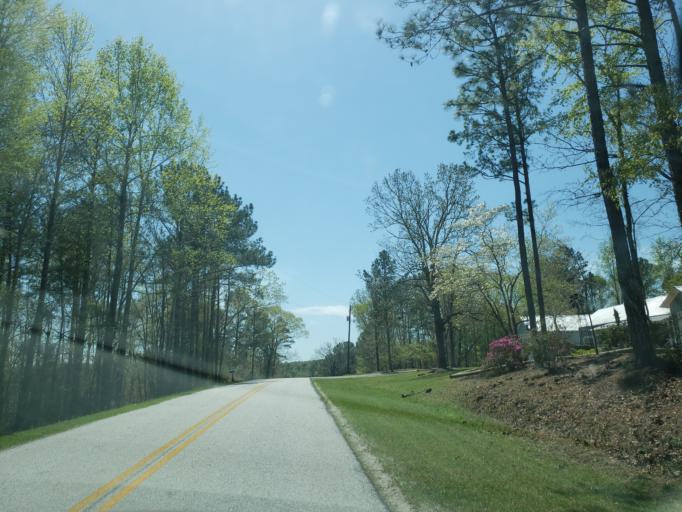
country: US
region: Alabama
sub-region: Elmore County
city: Tallassee
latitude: 32.6783
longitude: -85.8633
